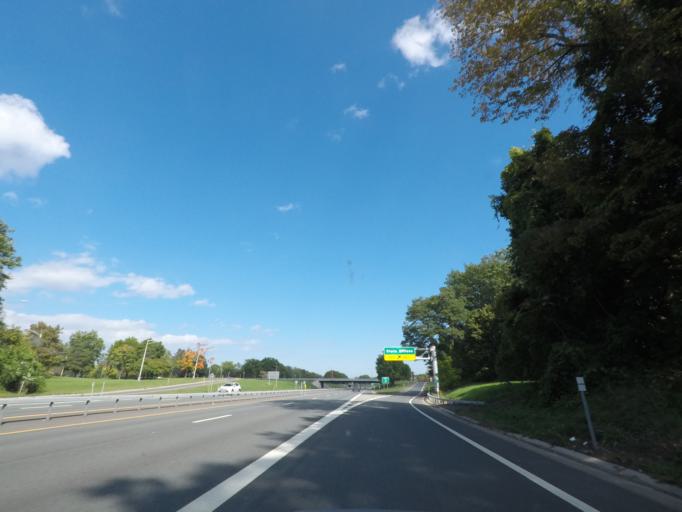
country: US
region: New York
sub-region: Albany County
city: Roessleville
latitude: 42.6715
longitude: -73.8086
